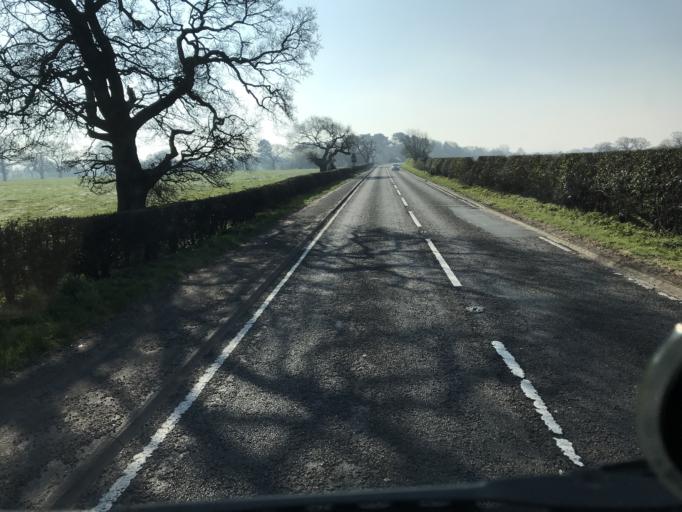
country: GB
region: England
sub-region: Cheshire West and Chester
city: Waverton
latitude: 53.1600
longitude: -2.8143
